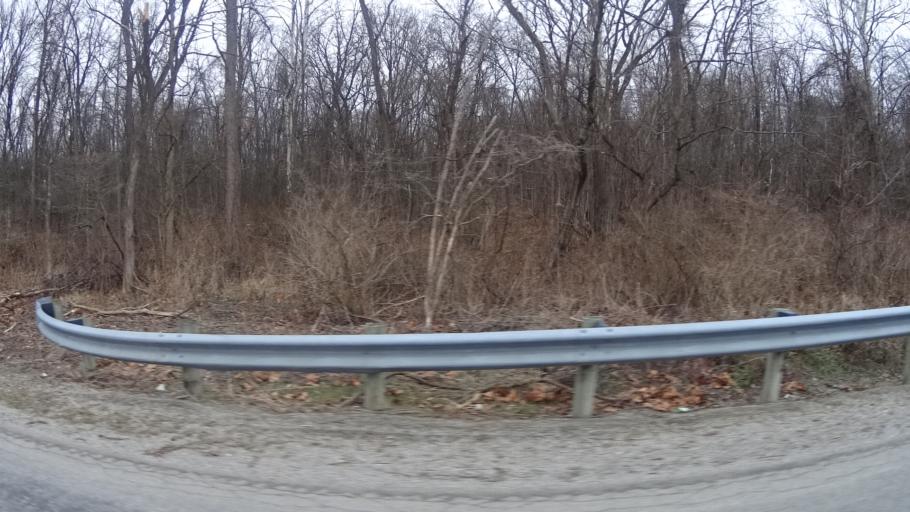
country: US
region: Ohio
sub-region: Lorain County
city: Wellington
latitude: 41.1484
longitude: -82.2463
